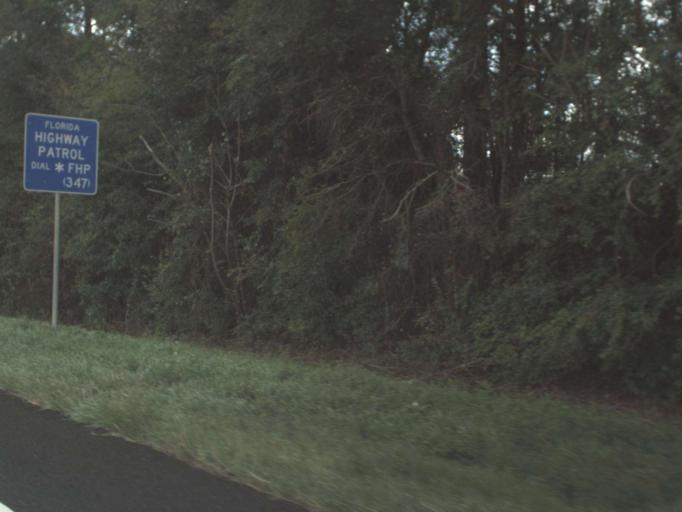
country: US
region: Florida
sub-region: Jackson County
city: Graceville
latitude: 30.9887
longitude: -85.4079
